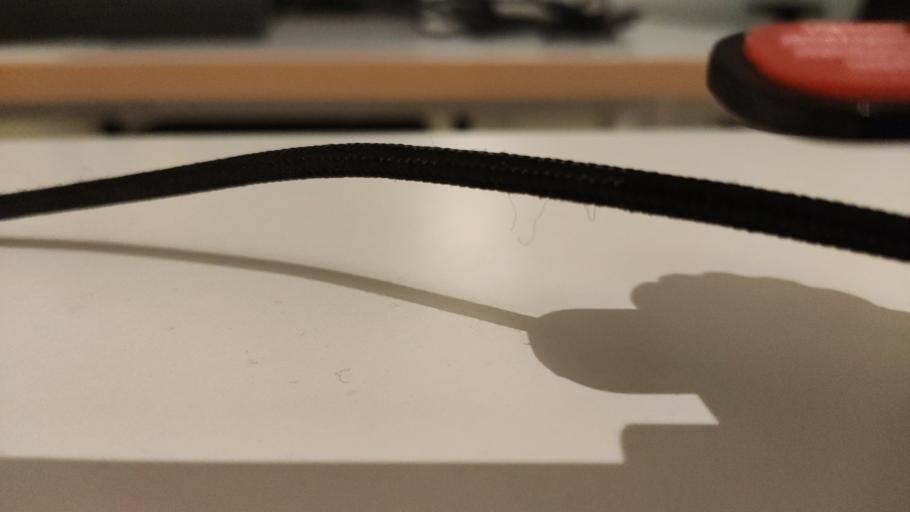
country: RU
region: Moskovskaya
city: Shaburnovo
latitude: 56.4228
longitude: 37.9702
